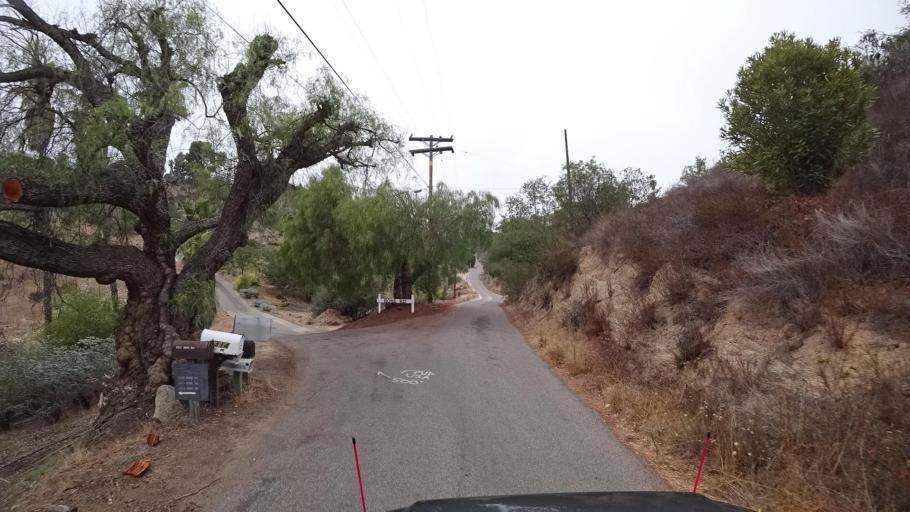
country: US
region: California
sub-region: San Diego County
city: Fallbrook
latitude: 33.4430
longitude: -117.2892
